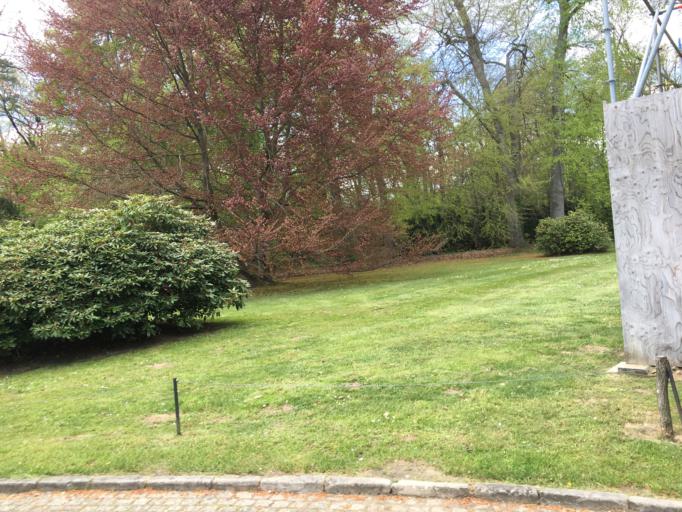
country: DE
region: Brandenburg
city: Potsdam
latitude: 52.4190
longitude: 13.0703
